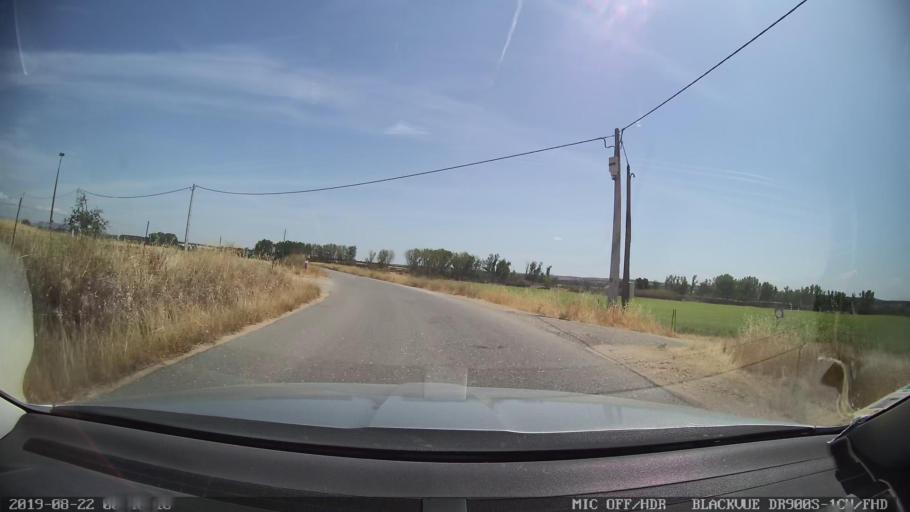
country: PT
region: Castelo Branco
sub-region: Idanha-A-Nova
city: Idanha-a-Nova
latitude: 39.8707
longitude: -7.1441
